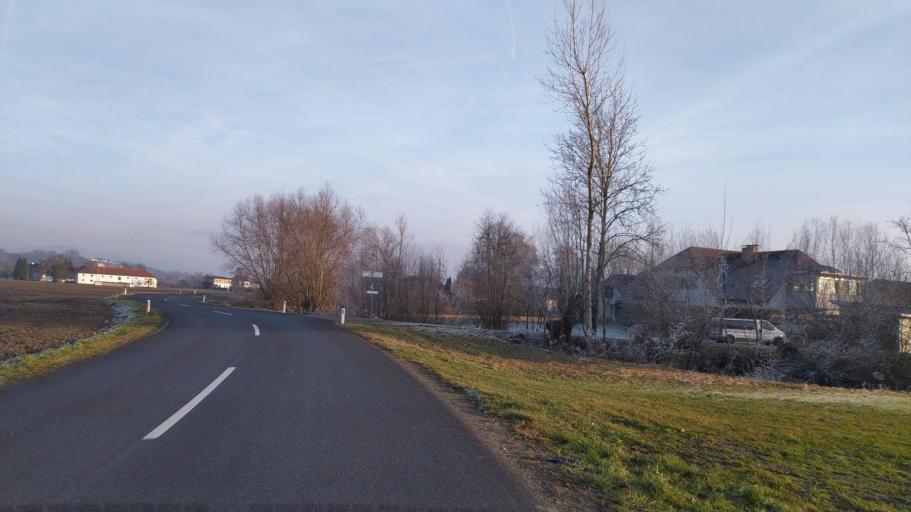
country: AT
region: Upper Austria
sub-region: Politischer Bezirk Urfahr-Umgebung
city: Goldworth
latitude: 48.3378
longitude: 14.0928
